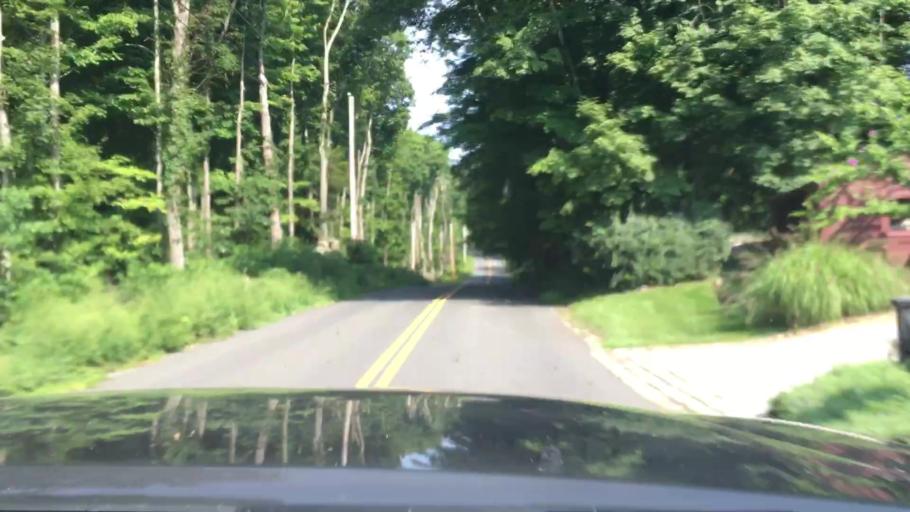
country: US
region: Connecticut
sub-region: Fairfield County
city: Georgetown
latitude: 41.2522
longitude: -73.4545
